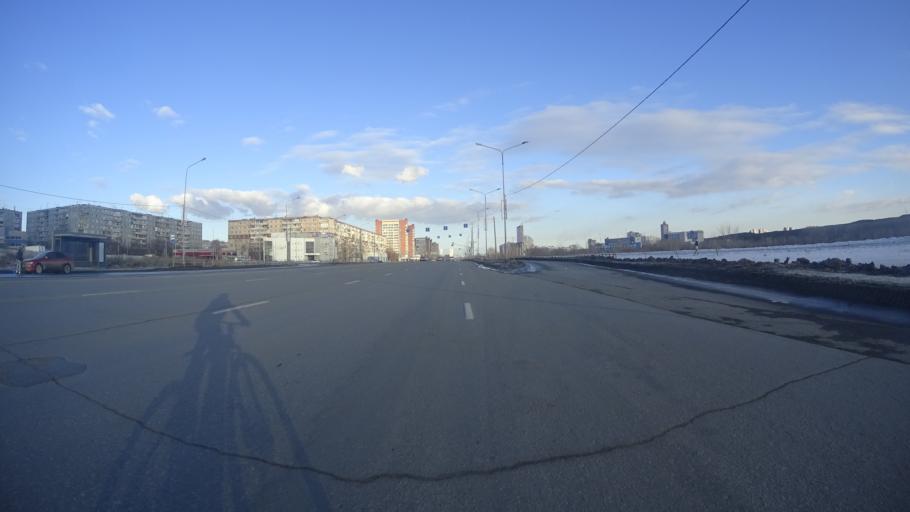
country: RU
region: Chelyabinsk
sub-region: Gorod Chelyabinsk
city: Chelyabinsk
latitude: 55.1743
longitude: 61.3322
